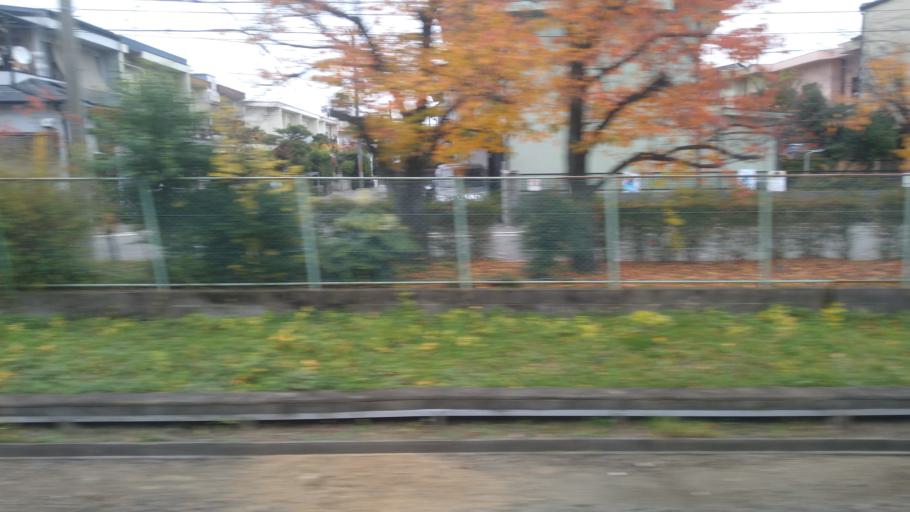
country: JP
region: Kyoto
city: Yawata
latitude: 34.9109
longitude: 135.6879
